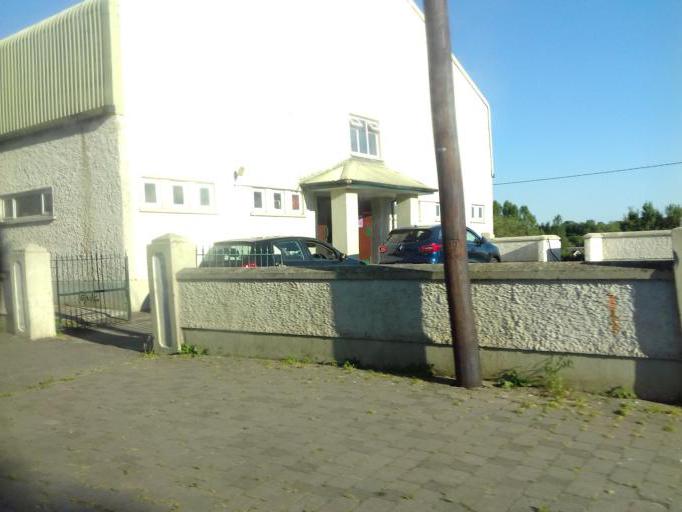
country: IE
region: Leinster
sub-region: Fingal County
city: Swords
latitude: 53.4902
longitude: -6.3017
